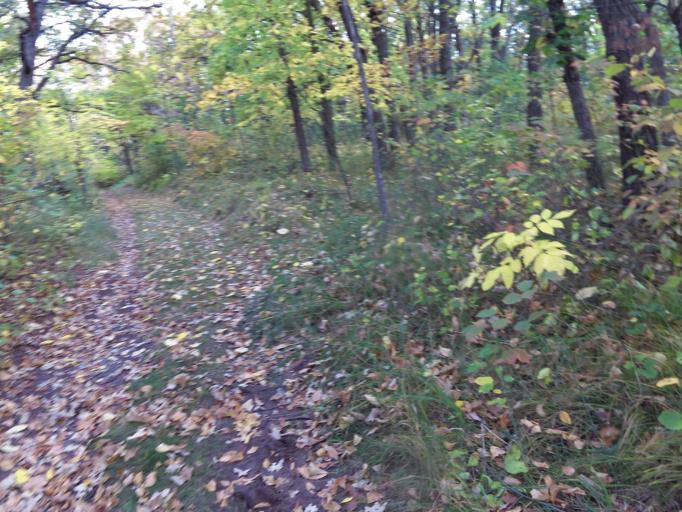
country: US
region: North Dakota
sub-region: Pembina County
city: Cavalier
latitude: 48.7788
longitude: -97.7316
